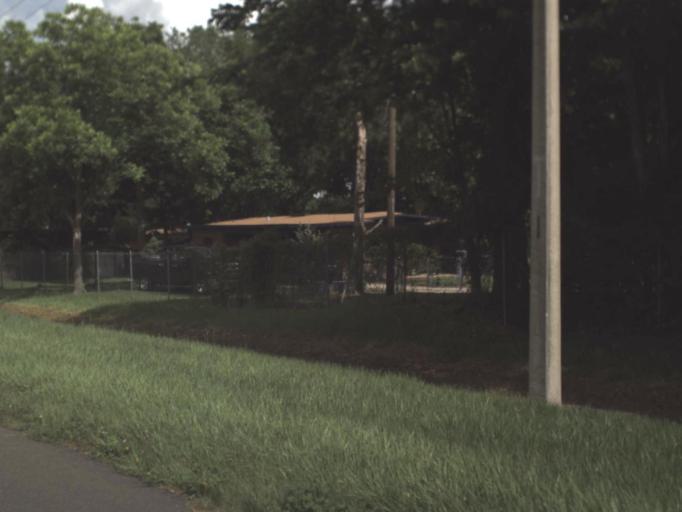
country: US
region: Florida
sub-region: Duval County
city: Jacksonville
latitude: 30.3569
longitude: -81.7049
